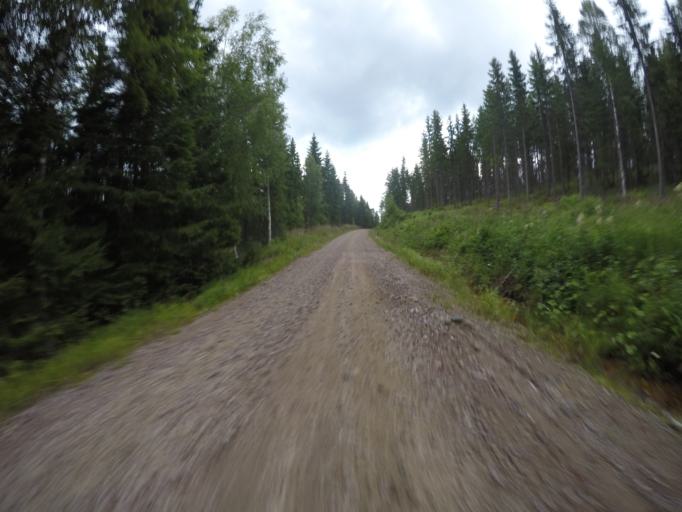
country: SE
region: Vaermland
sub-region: Filipstads Kommun
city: Lesjofors
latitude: 60.1990
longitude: 14.3663
